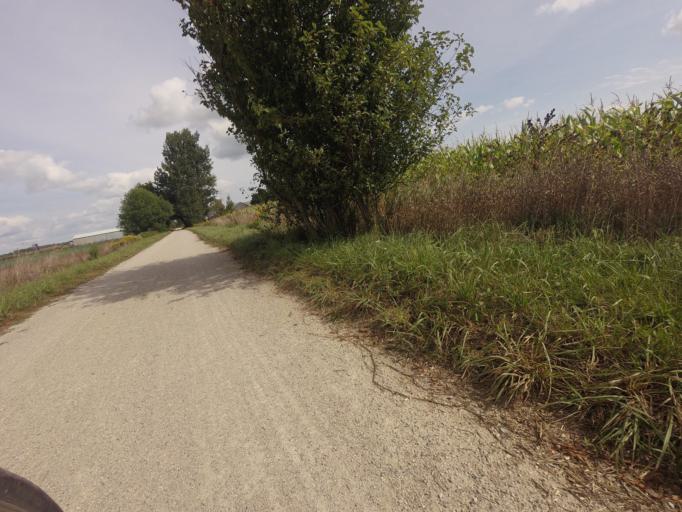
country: CA
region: Ontario
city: Waterloo
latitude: 43.6014
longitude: -80.5291
